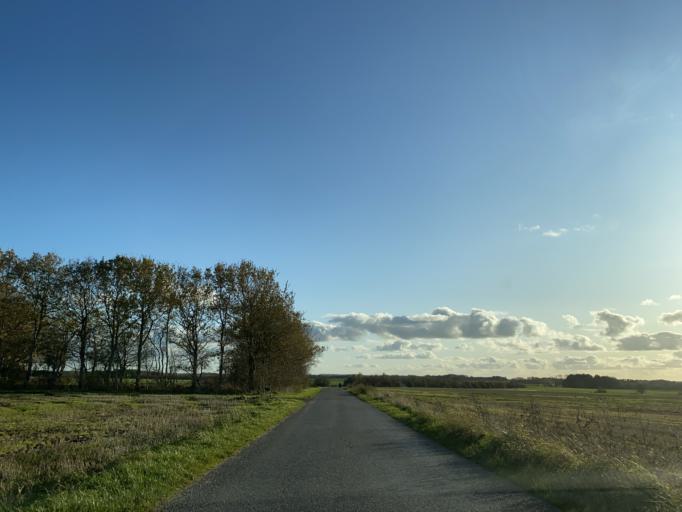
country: DK
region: Central Jutland
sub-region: Viborg Kommune
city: Bjerringbro
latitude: 56.3309
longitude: 9.7091
